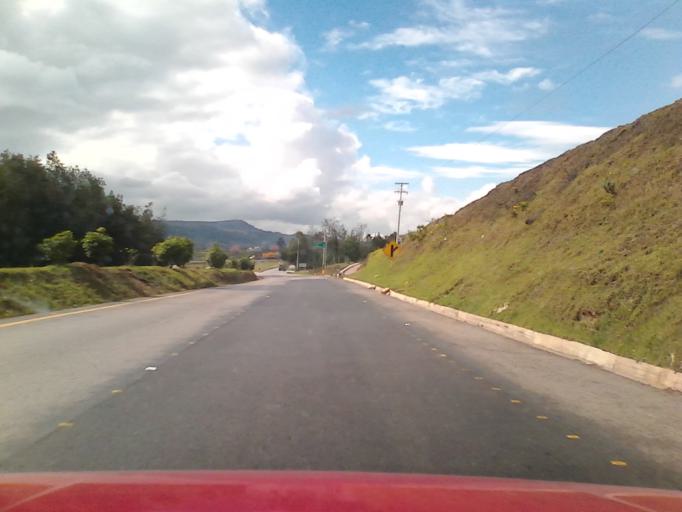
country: CO
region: Boyaca
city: Combita
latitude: 5.6067
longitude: -73.3256
